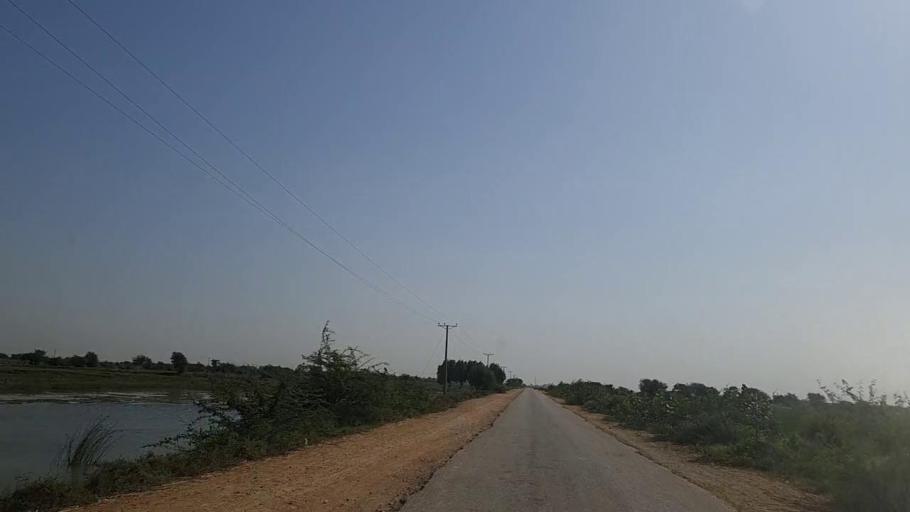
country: PK
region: Sindh
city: Mirpur Batoro
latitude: 24.6365
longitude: 68.2918
